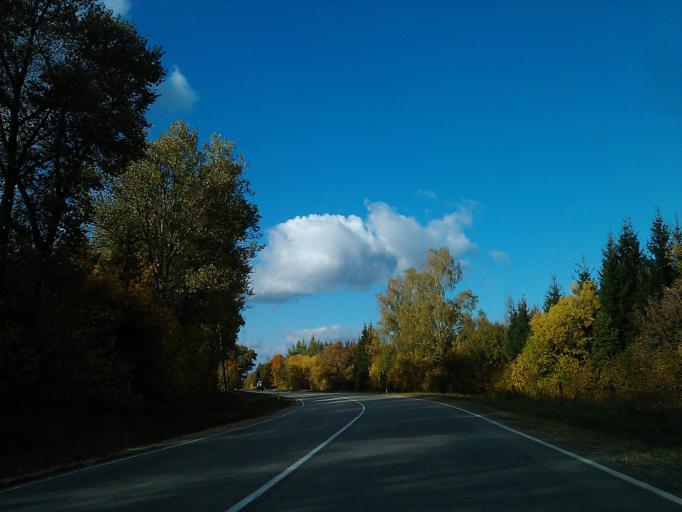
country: LV
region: Livani
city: Livani
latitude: 56.4402
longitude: 26.0707
